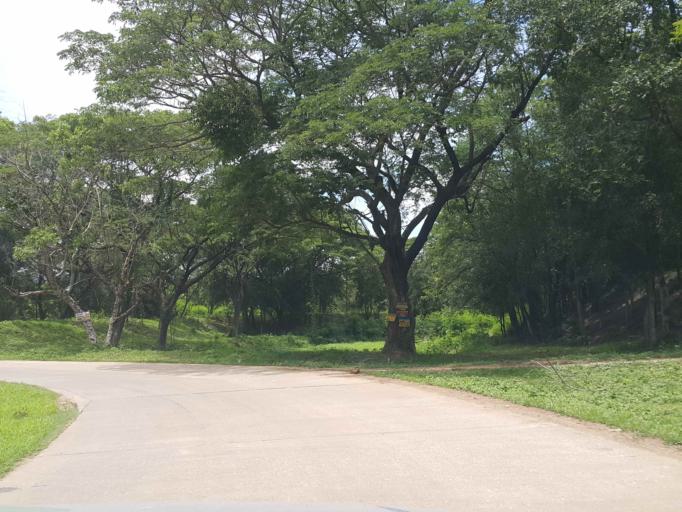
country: TH
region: Sukhothai
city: Ban Na
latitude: 17.0112
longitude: 99.7064
